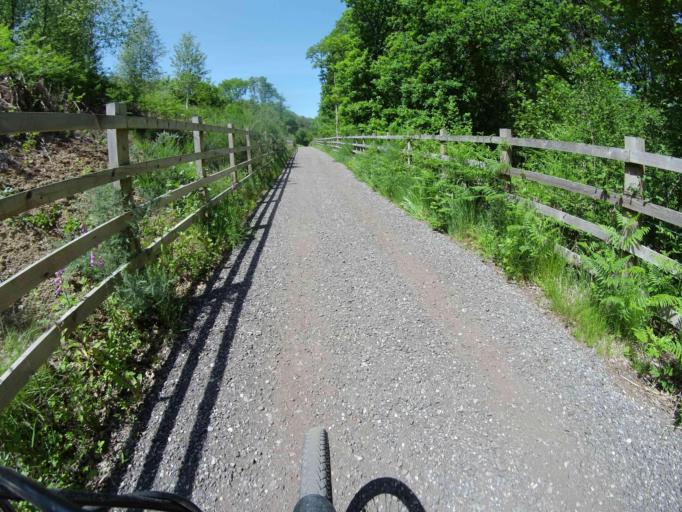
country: GB
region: England
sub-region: Devon
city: Bovey Tracey
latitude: 50.6367
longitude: -3.7330
